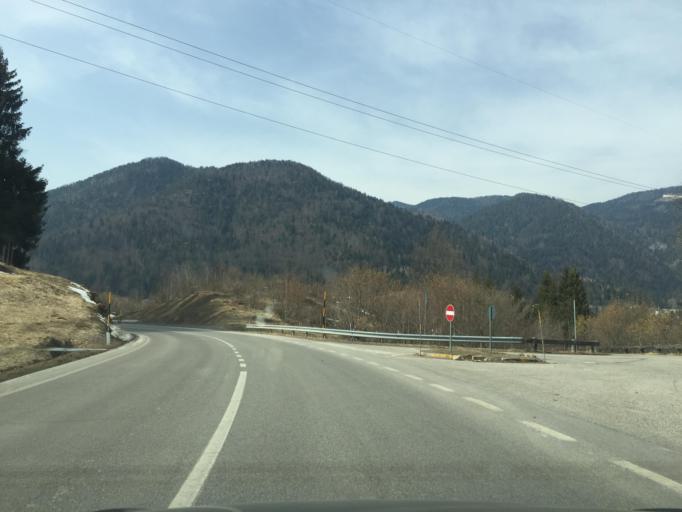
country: IT
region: Friuli Venezia Giulia
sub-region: Provincia di Udine
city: Tarvisio
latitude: 46.5078
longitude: 13.6130
